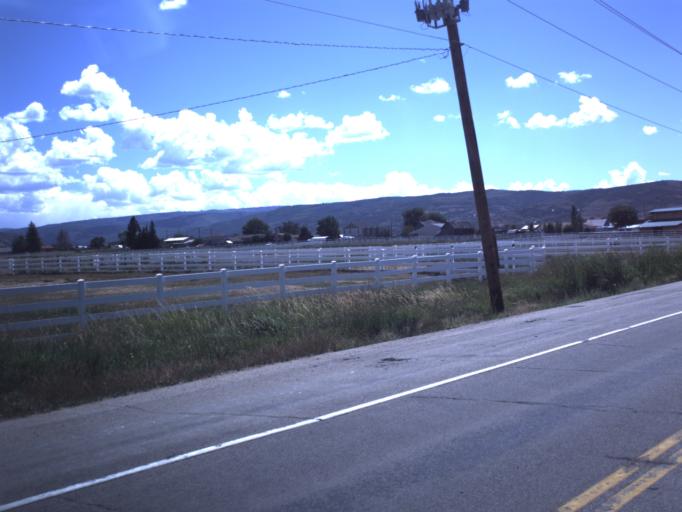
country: US
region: Utah
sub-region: Summit County
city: Francis
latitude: 40.6139
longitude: -111.2807
